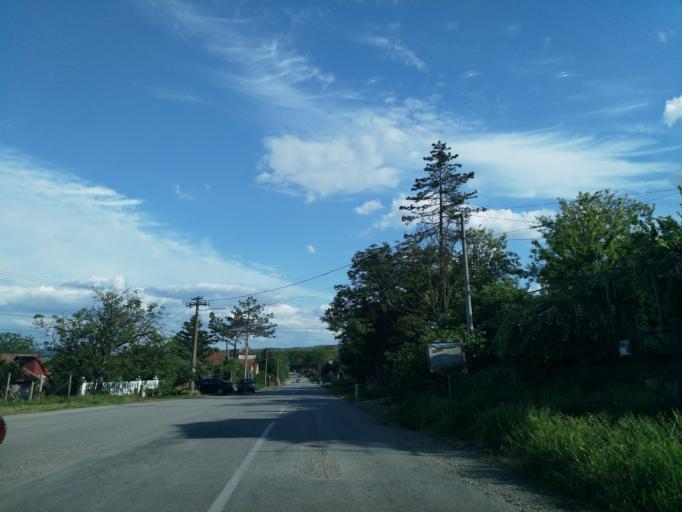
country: RS
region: Central Serbia
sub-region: Sumadijski Okrug
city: Batocina
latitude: 44.1610
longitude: 21.0983
